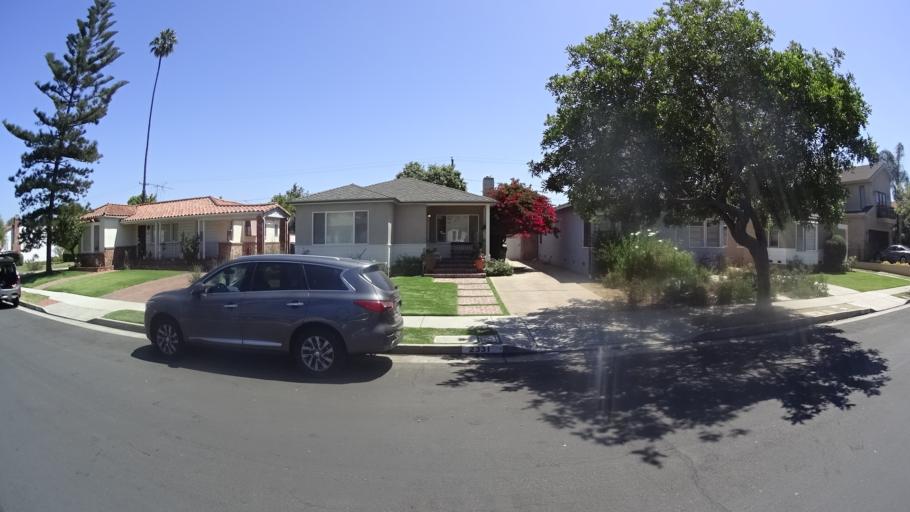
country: US
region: California
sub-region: Los Angeles County
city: Santa Monica
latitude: 34.0232
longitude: -118.4581
